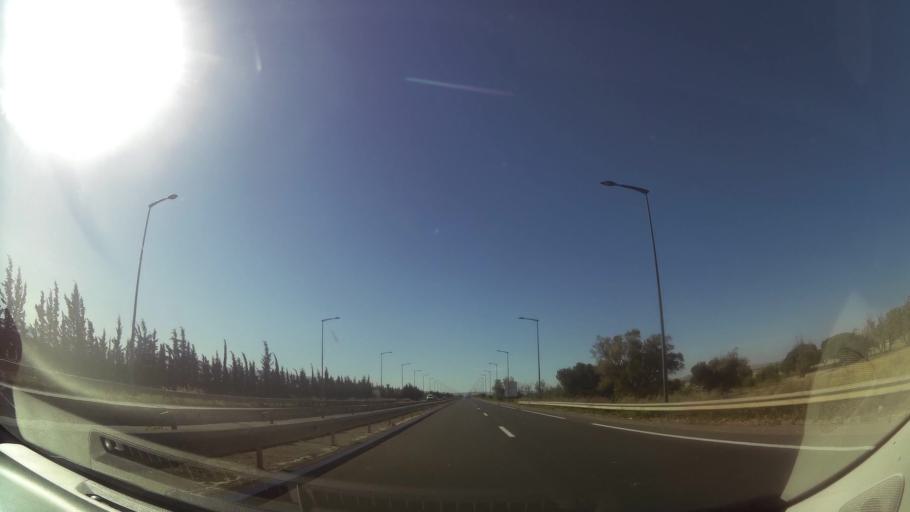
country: MA
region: Oriental
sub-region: Oujda-Angad
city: Oujda
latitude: 34.8121
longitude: -1.9622
